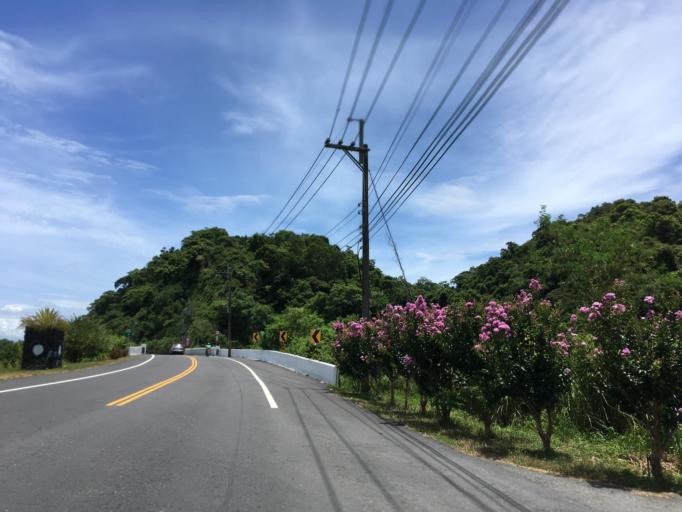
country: TW
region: Taiwan
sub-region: Yilan
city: Yilan
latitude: 24.6434
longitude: 121.7216
